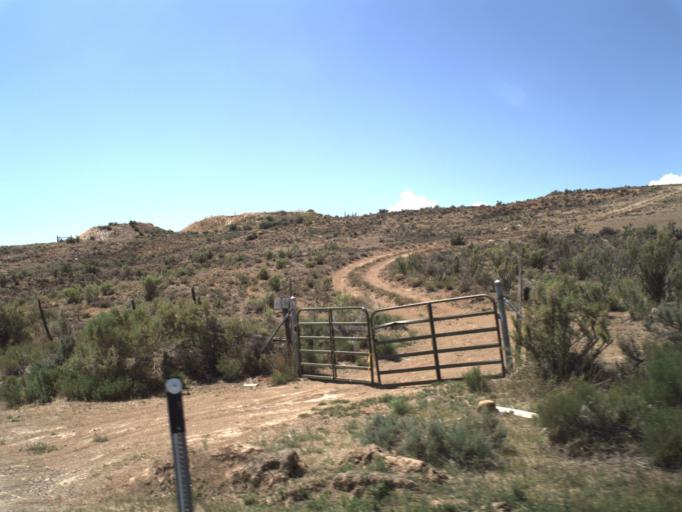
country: US
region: Utah
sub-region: Rich County
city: Randolph
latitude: 41.5235
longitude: -111.1857
